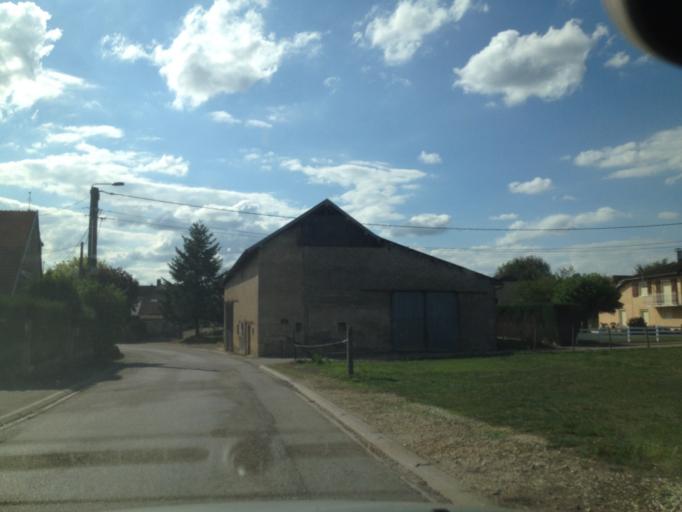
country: FR
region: Franche-Comte
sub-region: Departement de la Haute-Saone
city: Faverney
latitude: 47.8106
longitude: 6.1330
